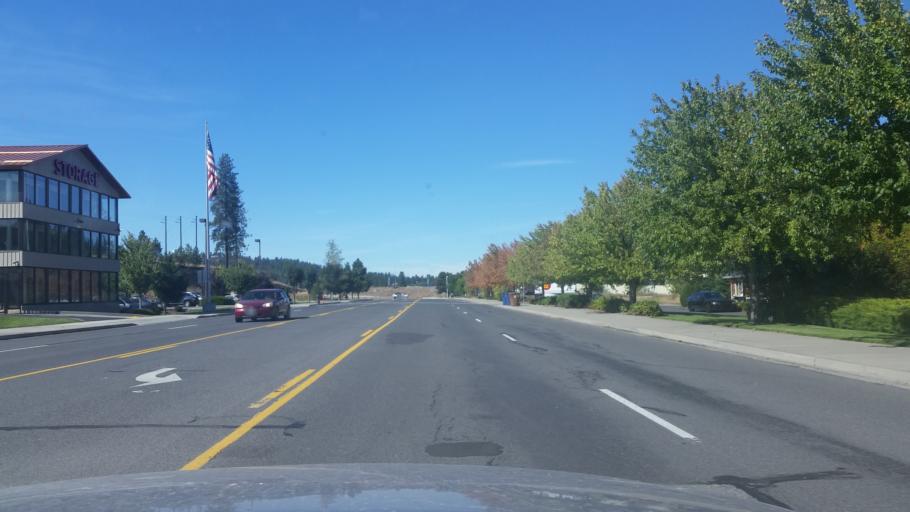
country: US
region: Washington
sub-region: Spokane County
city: Spokane
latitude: 47.6156
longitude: -117.4309
